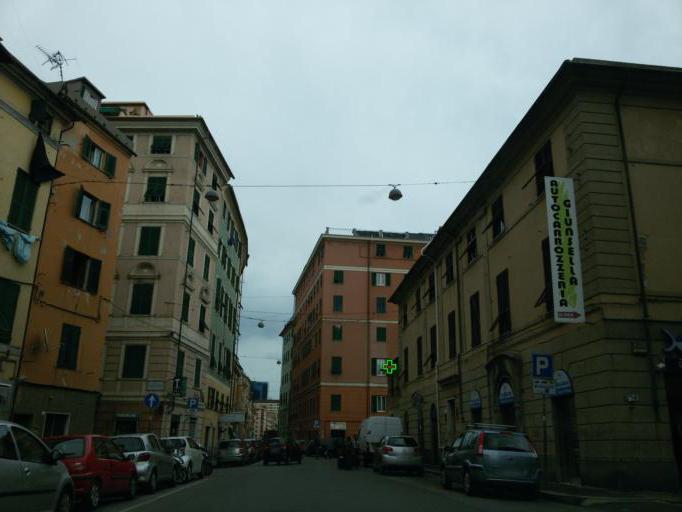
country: IT
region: Liguria
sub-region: Provincia di Genova
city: San Teodoro
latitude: 44.4097
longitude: 8.8906
